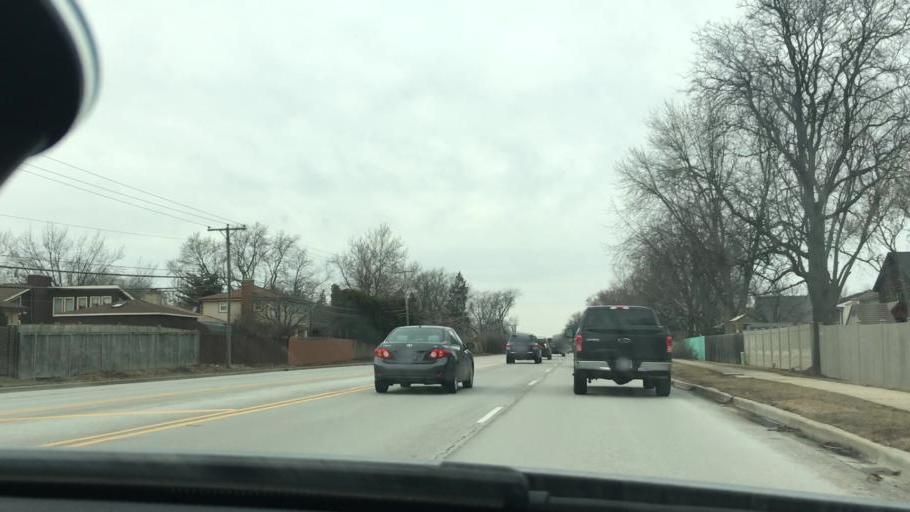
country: US
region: Illinois
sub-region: Cook County
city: Mount Prospect
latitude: 42.0617
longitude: -87.9116
